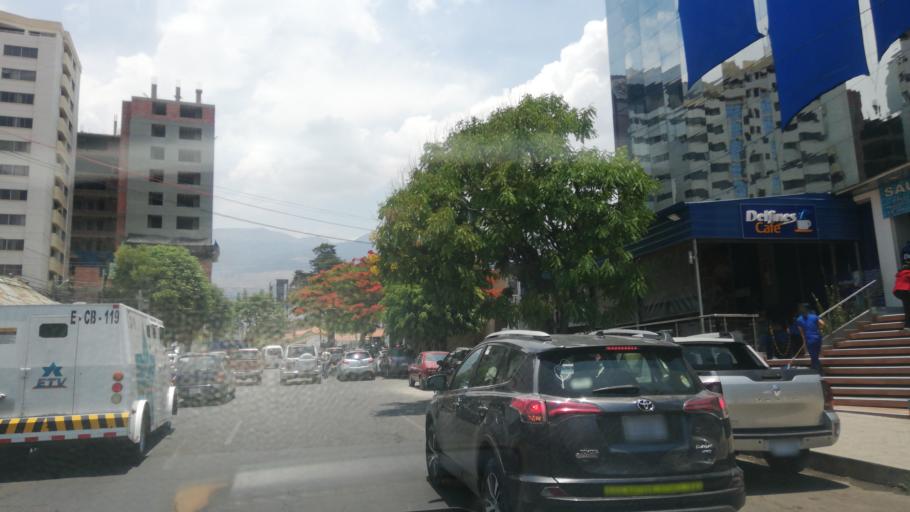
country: BO
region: Cochabamba
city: Cochabamba
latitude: -17.3733
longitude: -66.1607
